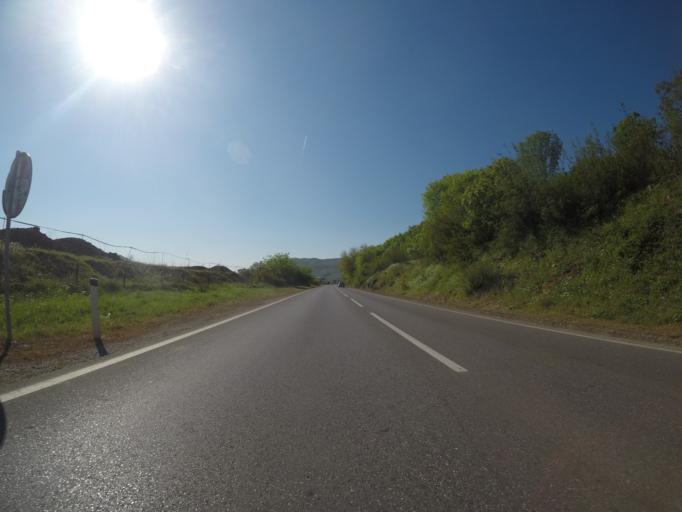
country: ME
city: Spuz
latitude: 42.4753
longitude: 19.1715
